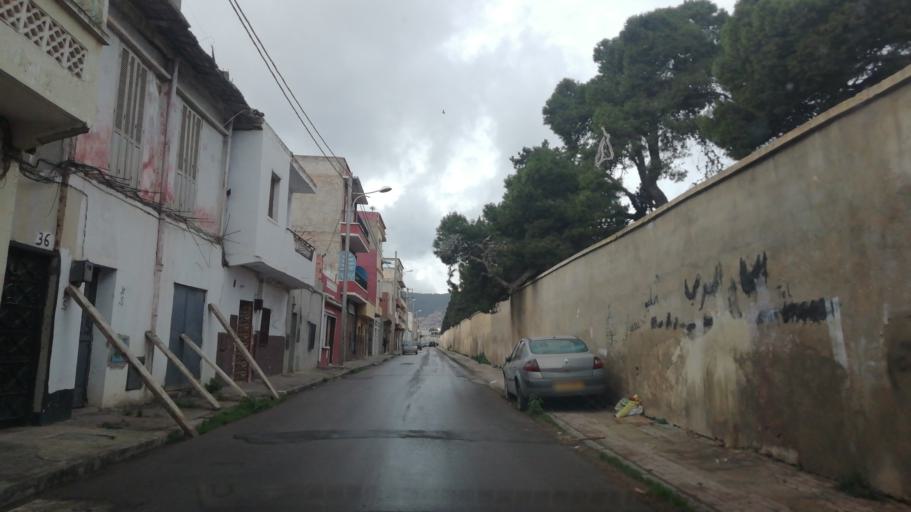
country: DZ
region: Oran
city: Oran
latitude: 35.6901
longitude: -0.6373
